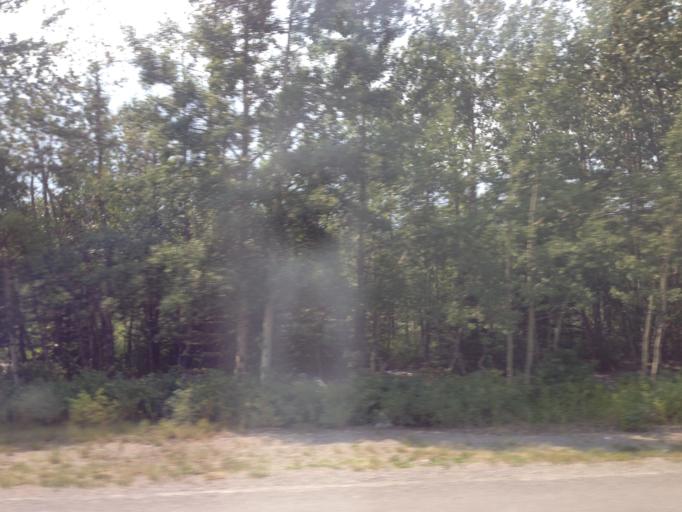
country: CA
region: Alberta
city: Canmore
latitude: 51.0791
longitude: -115.3398
